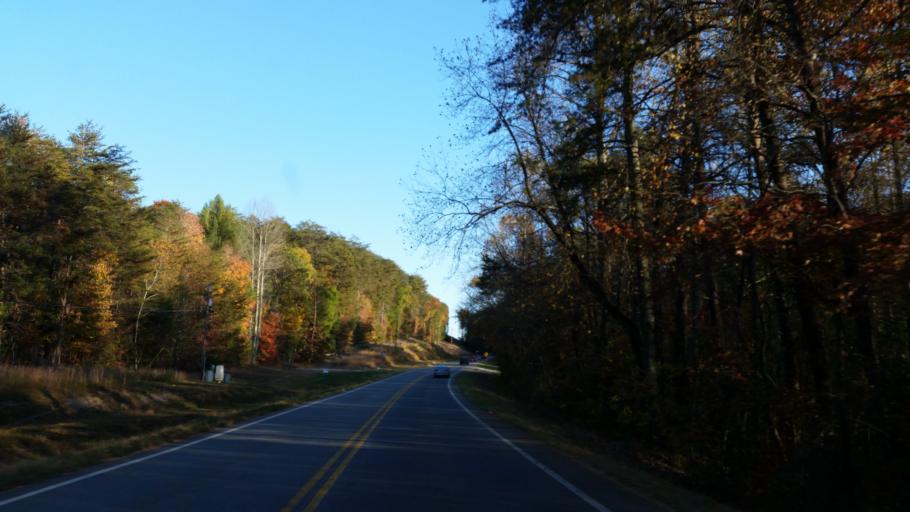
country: US
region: Georgia
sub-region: Pickens County
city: Jasper
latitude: 34.5469
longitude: -84.2791
